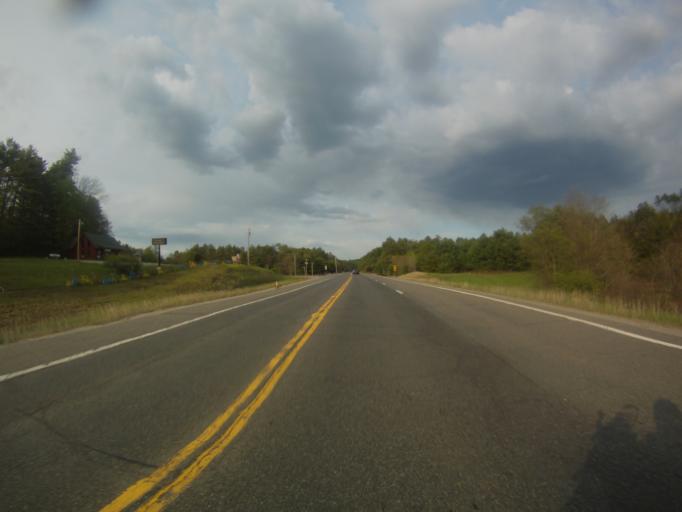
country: US
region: New York
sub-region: Warren County
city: Warrensburg
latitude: 43.6573
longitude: -73.7972
